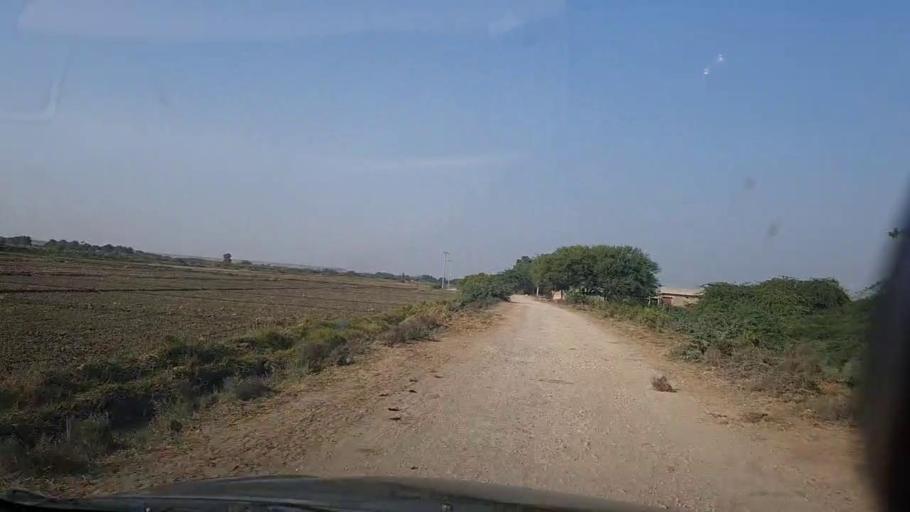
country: PK
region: Sindh
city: Thatta
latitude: 24.6019
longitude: 67.8743
